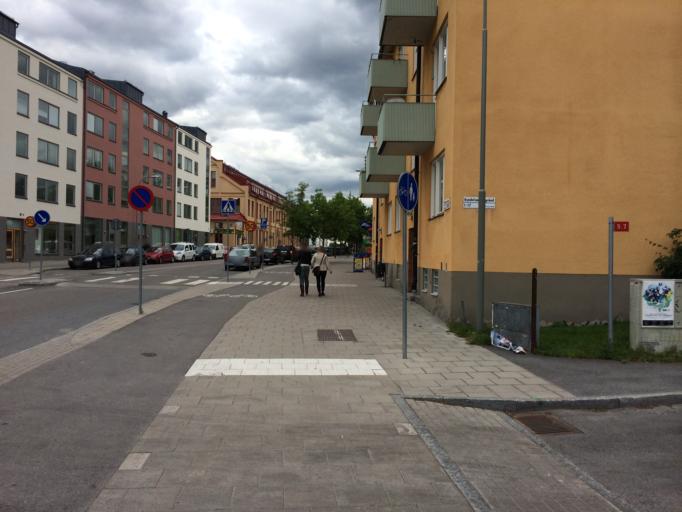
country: SE
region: Stockholm
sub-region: Stockholms Kommun
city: Arsta
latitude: 59.2999
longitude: 18.0039
